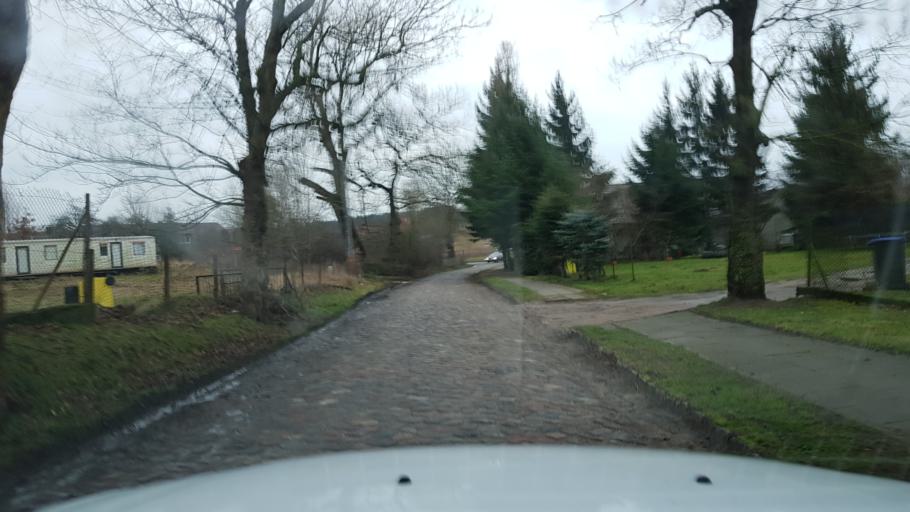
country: PL
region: West Pomeranian Voivodeship
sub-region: Powiat kolobrzeski
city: Grzybowo
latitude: 54.1339
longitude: 15.4825
